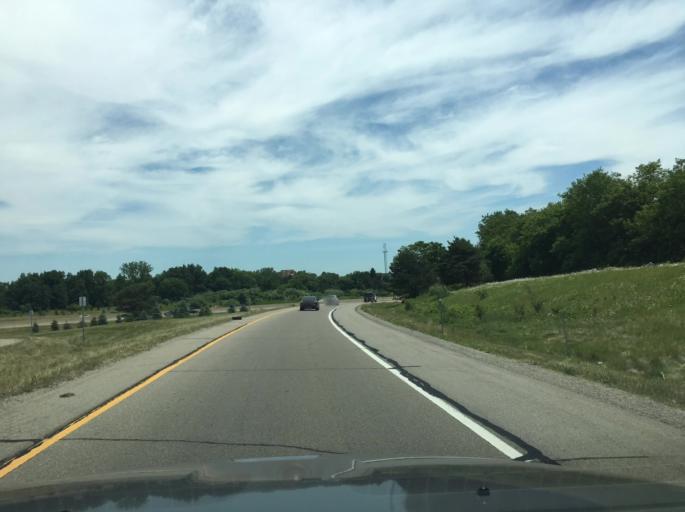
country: US
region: Michigan
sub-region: Oakland County
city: Auburn Hills
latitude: 42.6401
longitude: -83.2367
